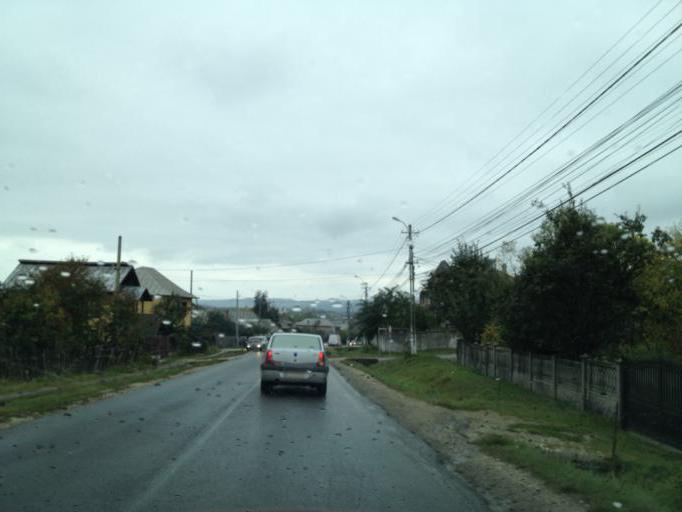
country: RO
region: Arges
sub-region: Comuna Valea Mare-Pravat
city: Valea Mare Pravat
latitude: 45.2961
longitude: 25.1029
